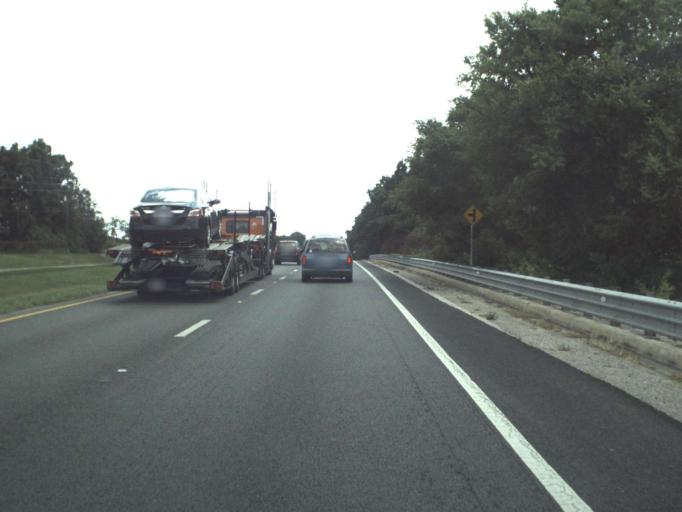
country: US
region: Florida
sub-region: Marion County
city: Citra
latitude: 29.3077
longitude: -82.1519
